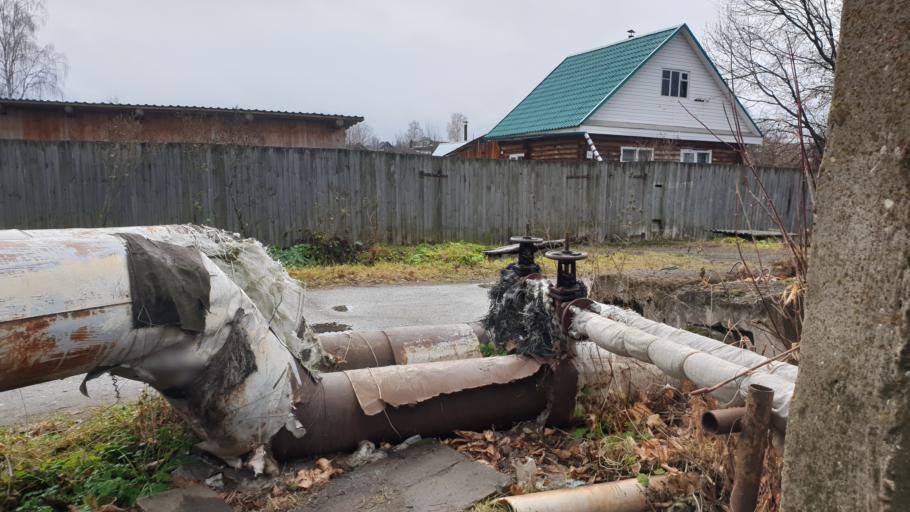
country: RU
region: Kirov
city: Kirs
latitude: 59.3348
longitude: 52.2394
